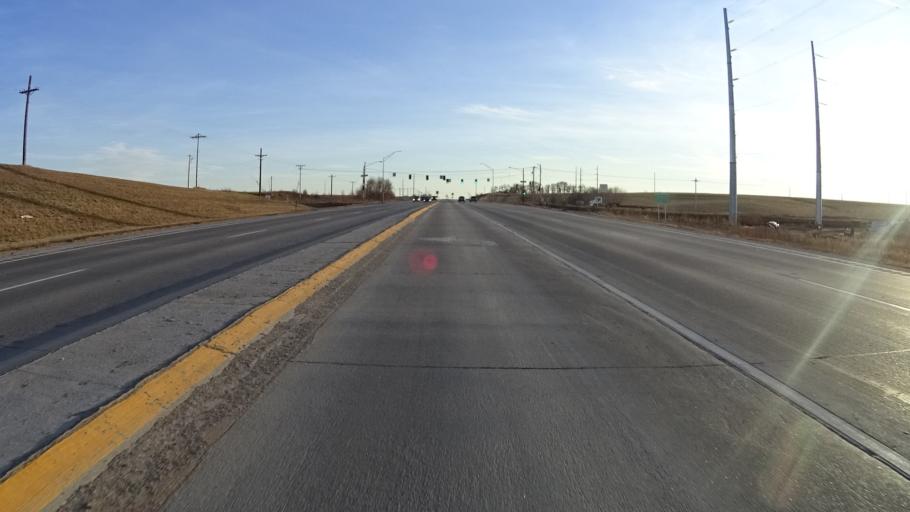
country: US
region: Nebraska
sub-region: Sarpy County
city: Chalco
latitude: 41.1339
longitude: -96.1391
